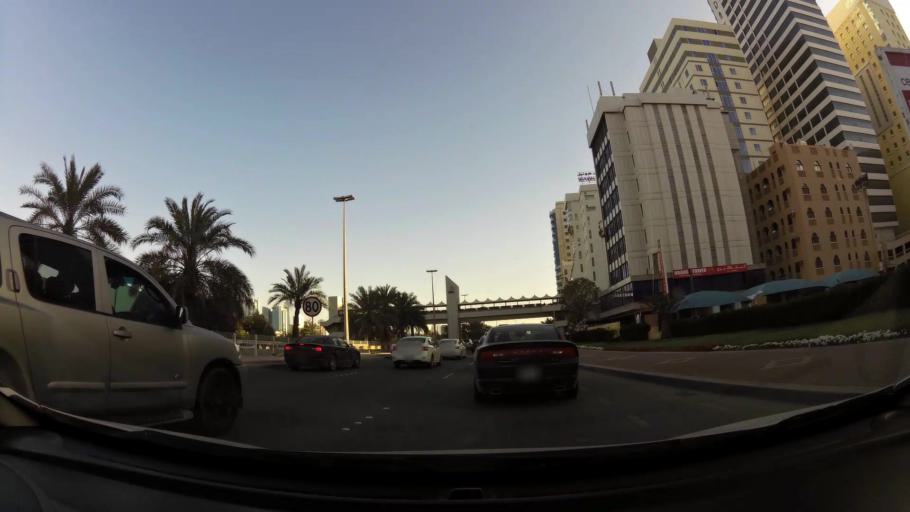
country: BH
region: Manama
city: Manama
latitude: 26.2329
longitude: 50.5983
